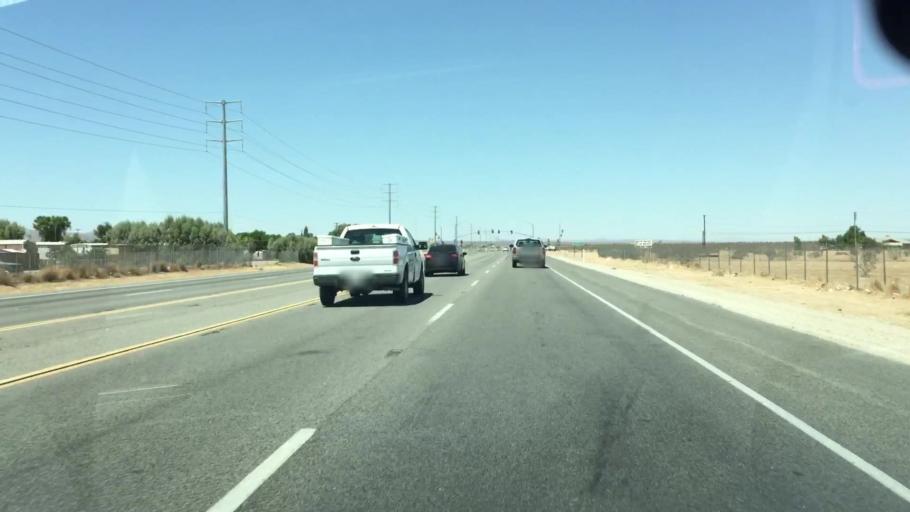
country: US
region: California
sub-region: San Bernardino County
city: Adelanto
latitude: 34.5838
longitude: -117.4136
